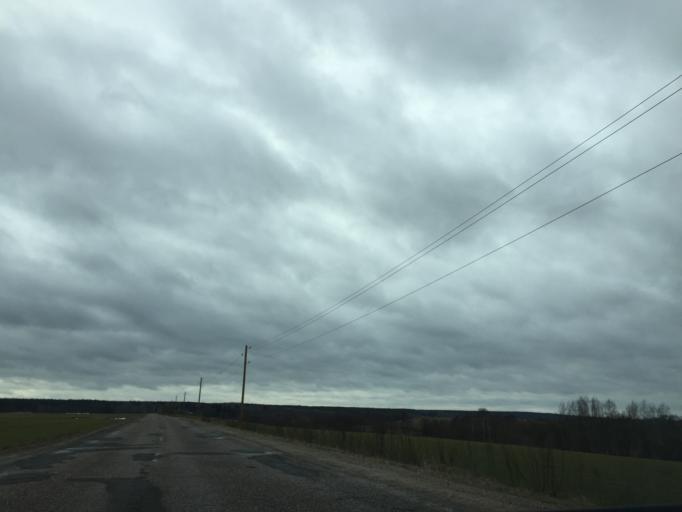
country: LV
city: Tervete
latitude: 56.5045
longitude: 23.4588
